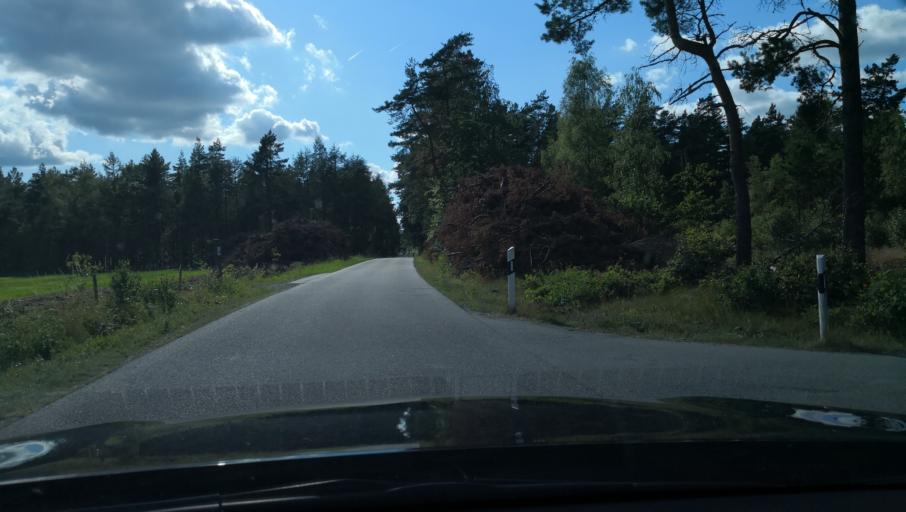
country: SE
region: Skane
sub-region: Simrishamns Kommun
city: Kivik
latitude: 55.7685
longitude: 14.1826
